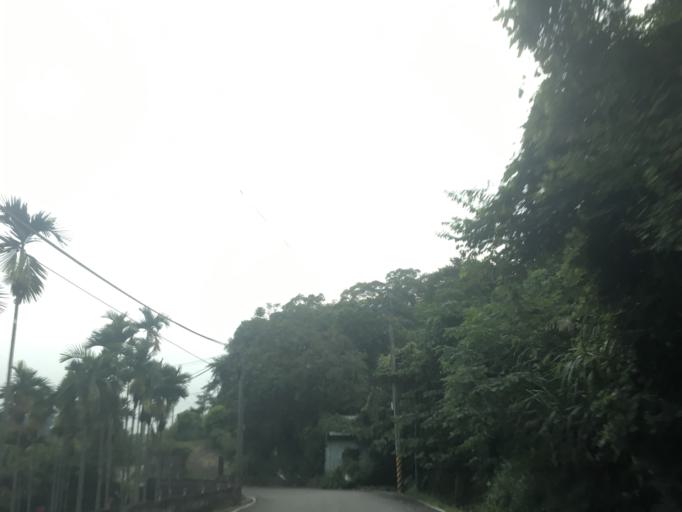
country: TW
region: Taiwan
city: Fengyuan
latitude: 24.1890
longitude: 120.7791
